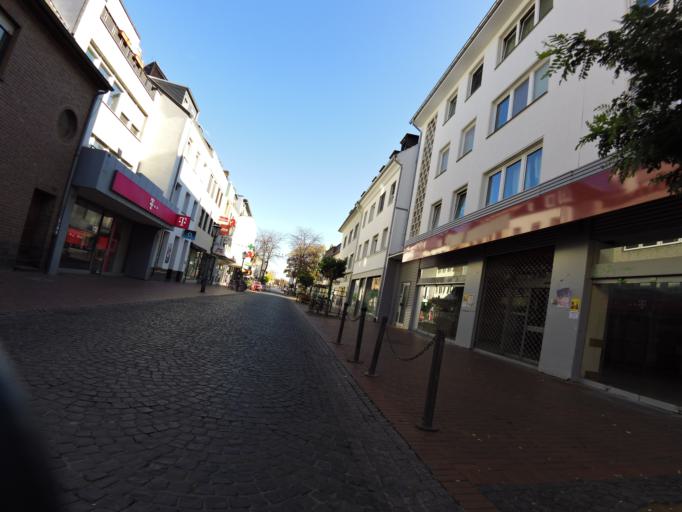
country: DE
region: North Rhine-Westphalia
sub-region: Regierungsbezirk Koln
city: Alfter
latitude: 50.7151
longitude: 7.0488
